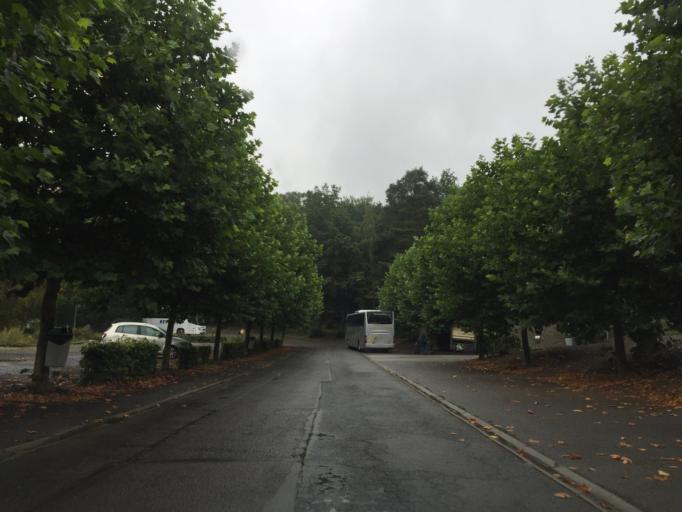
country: BE
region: Wallonia
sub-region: Province de Liege
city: Spa
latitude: 50.4971
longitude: 5.8645
